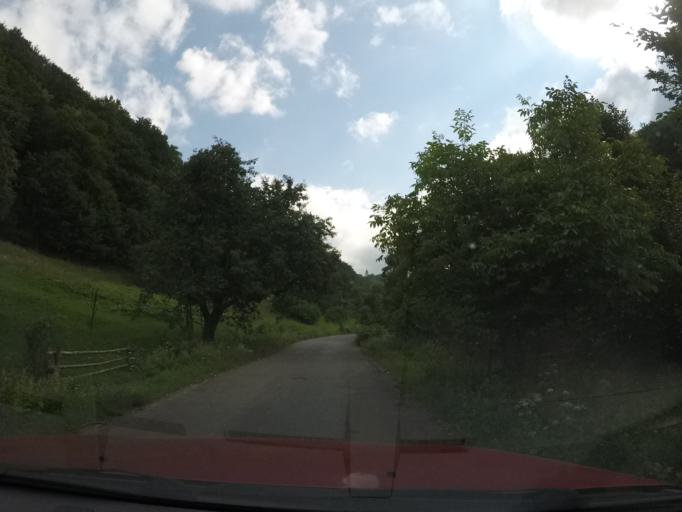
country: UA
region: Zakarpattia
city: Velykyi Bereznyi
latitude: 48.9460
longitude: 22.6415
